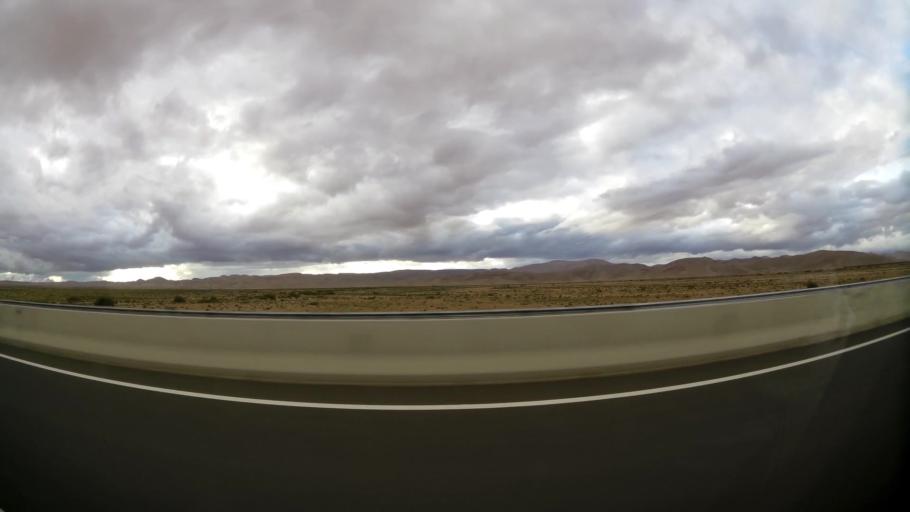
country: MA
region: Taza-Al Hoceima-Taounate
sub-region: Taza
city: Guercif
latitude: 34.3185
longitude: -3.5831
